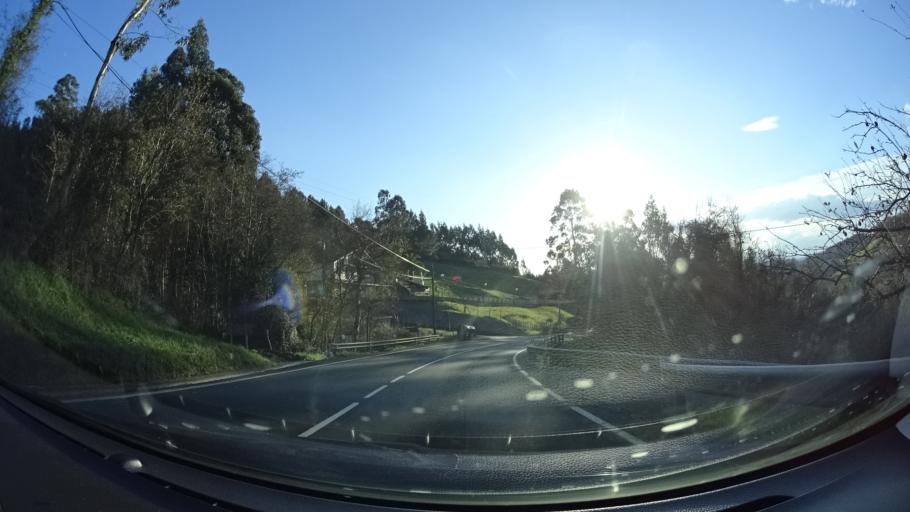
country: ES
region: Basque Country
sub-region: Bizkaia
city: Mungia
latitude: 43.3780
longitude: -2.7932
